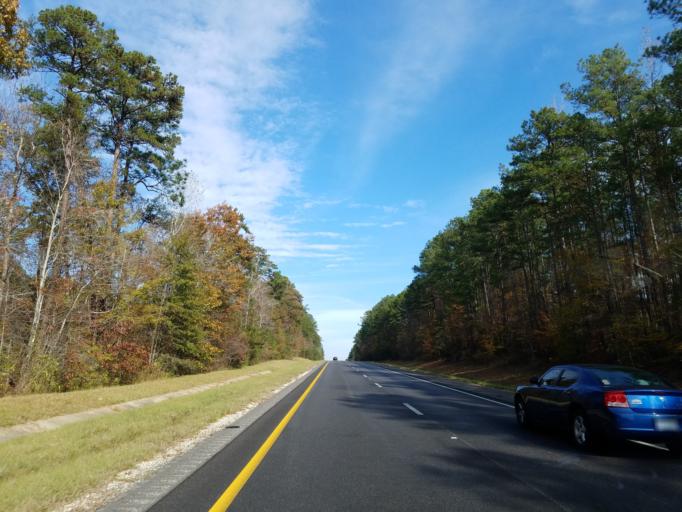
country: US
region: Mississippi
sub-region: Lauderdale County
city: Nellieburg
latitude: 32.3047
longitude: -88.8030
